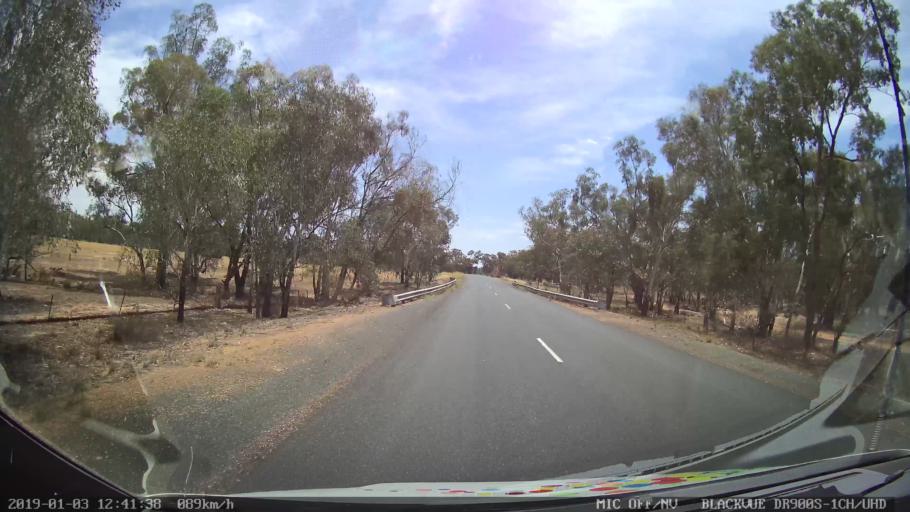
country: AU
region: New South Wales
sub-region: Weddin
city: Grenfell
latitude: -33.7971
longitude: 148.2153
